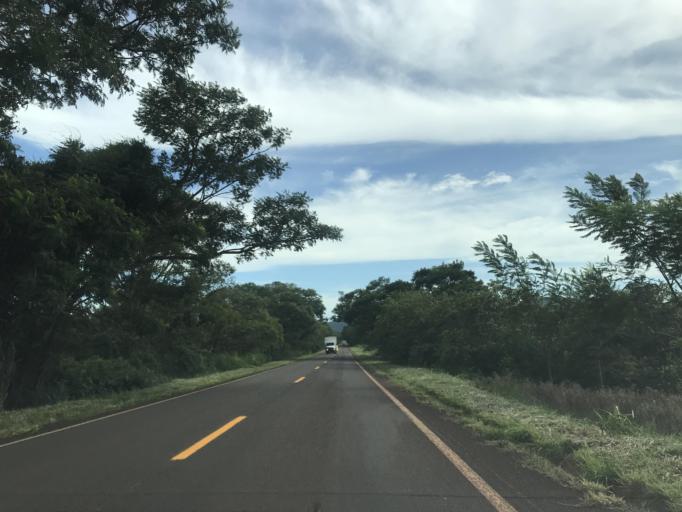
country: BR
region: Parana
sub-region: Paranavai
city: Nova Aurora
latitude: -22.8166
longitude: -52.6547
